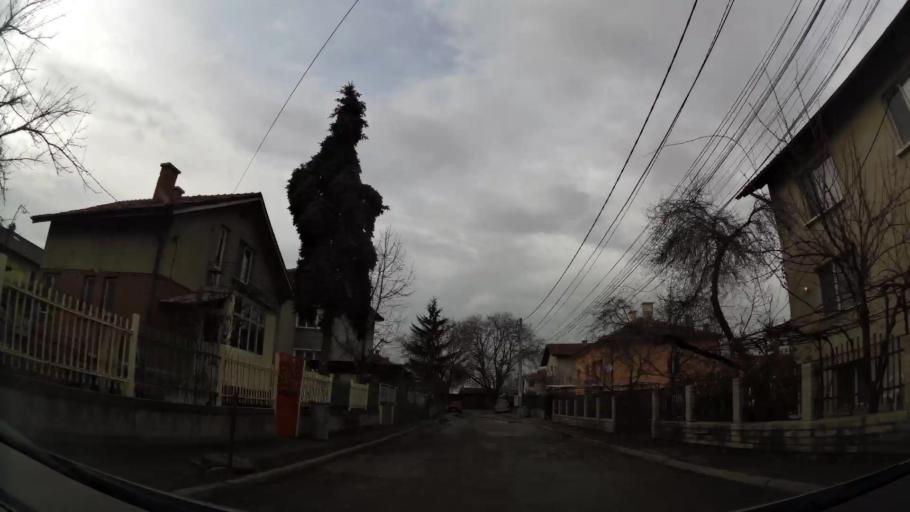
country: BG
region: Sofiya
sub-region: Obshtina Bozhurishte
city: Bozhurishte
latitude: 42.7440
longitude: 23.2621
